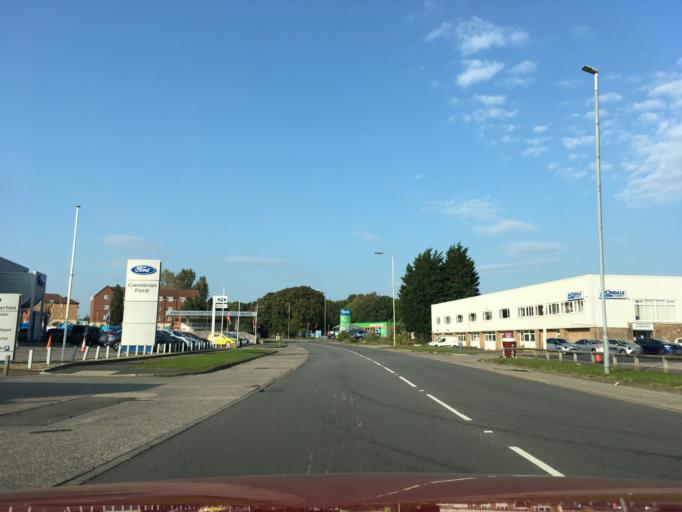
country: GB
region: Wales
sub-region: Torfaen County Borough
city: Cwmbran
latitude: 51.6606
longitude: -3.0180
